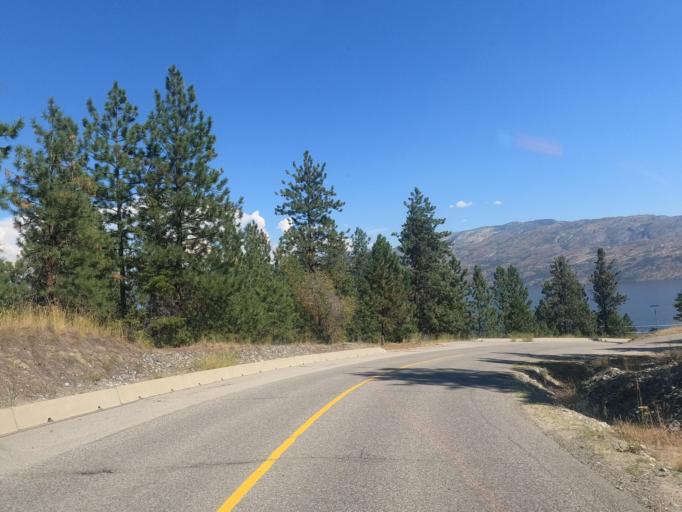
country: CA
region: British Columbia
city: Peachland
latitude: 49.7908
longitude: -119.7096
